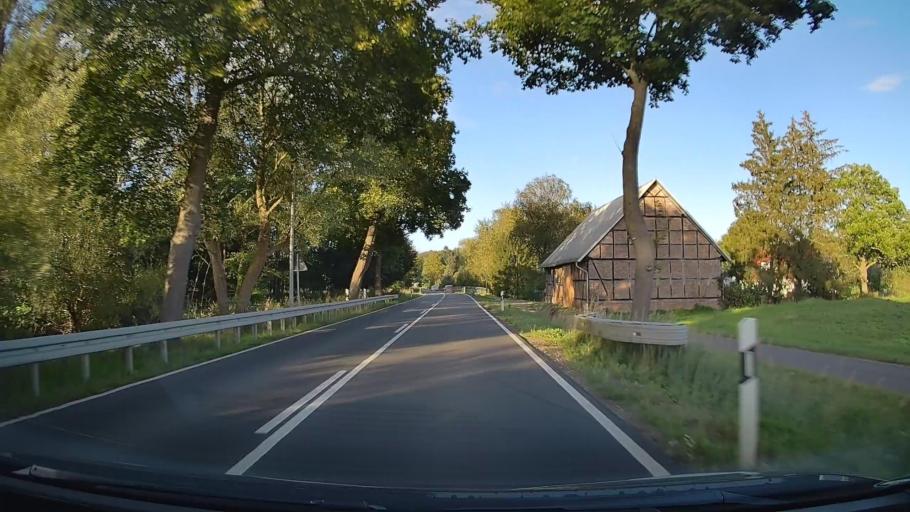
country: DE
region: Mecklenburg-Vorpommern
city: Steinhagen
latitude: 54.2426
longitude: 13.0147
